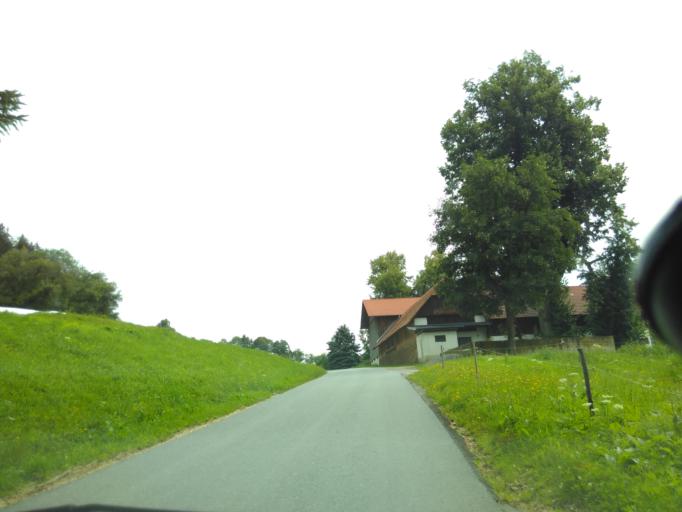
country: AT
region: Styria
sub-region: Politischer Bezirk Graz-Umgebung
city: Semriach
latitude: 47.2456
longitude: 15.3958
